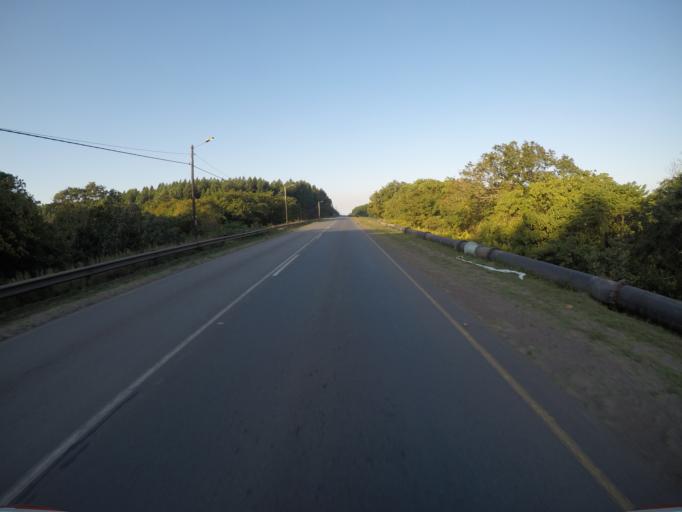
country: ZA
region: KwaZulu-Natal
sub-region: uThungulu District Municipality
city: KwaMbonambi
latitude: -28.6833
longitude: 32.1538
